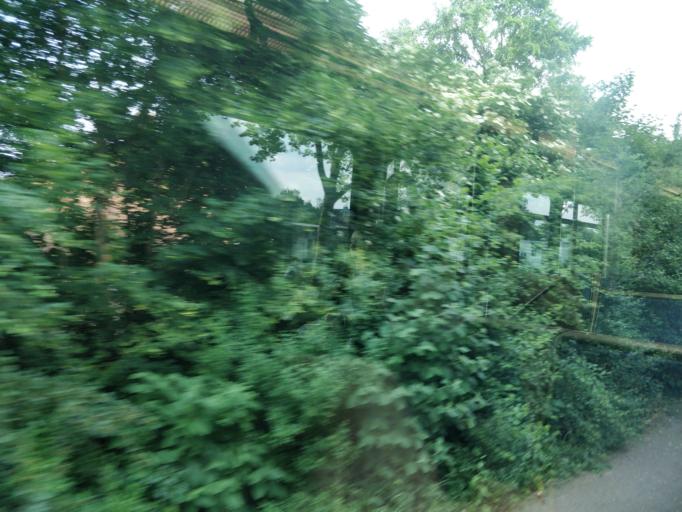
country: DE
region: North Rhine-Westphalia
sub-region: Regierungsbezirk Koln
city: Bilderstoeckchen
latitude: 50.9750
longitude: 6.9044
